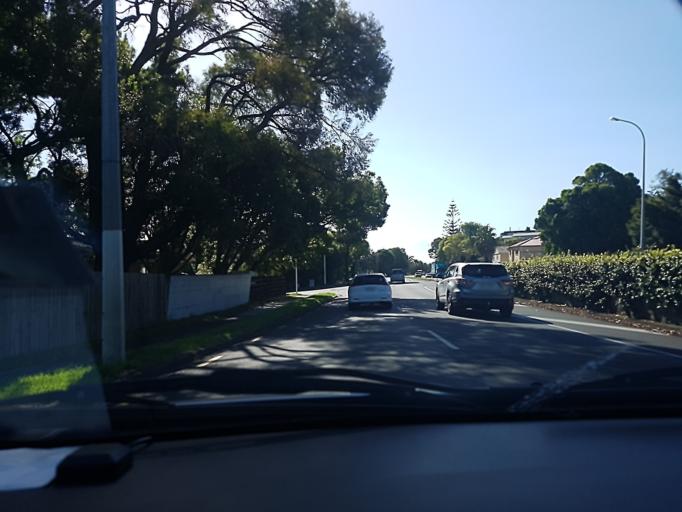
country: NZ
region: Auckland
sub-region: Auckland
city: Tamaki
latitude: -36.9226
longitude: 174.8803
